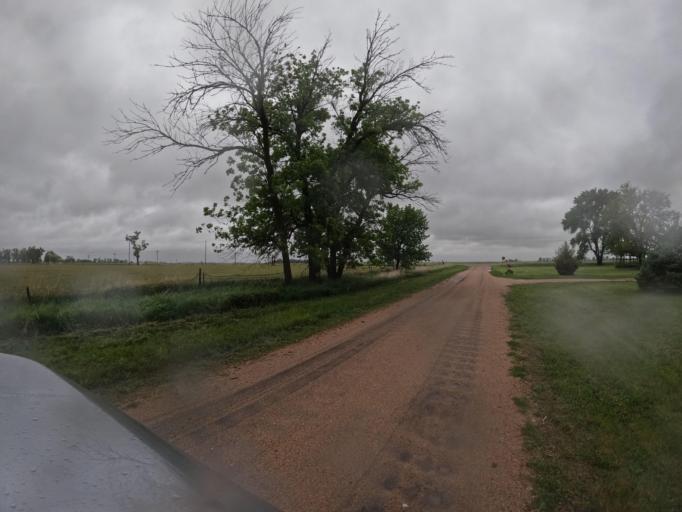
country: US
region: Nebraska
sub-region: Clay County
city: Harvard
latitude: 40.6122
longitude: -98.0986
